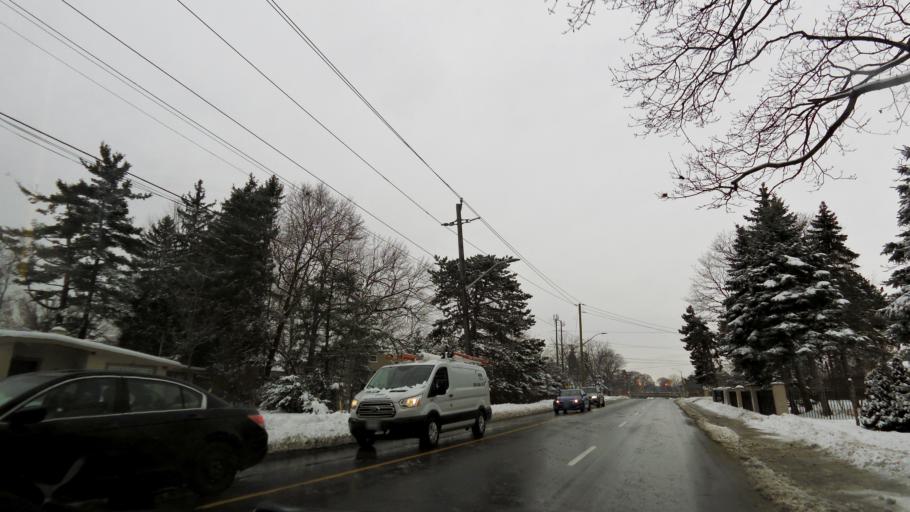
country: CA
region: Ontario
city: Mississauga
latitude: 43.5519
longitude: -79.6100
